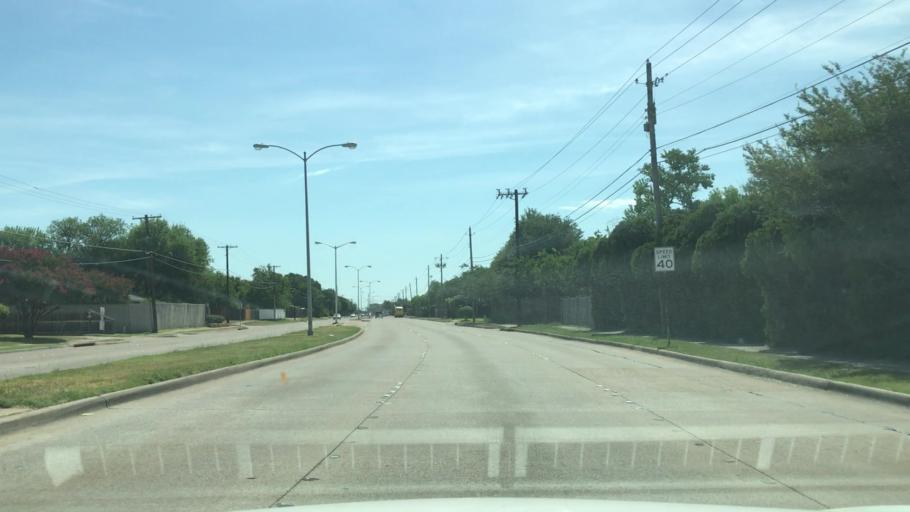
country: US
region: Texas
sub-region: Dallas County
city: Garland
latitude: 32.9308
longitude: -96.6388
